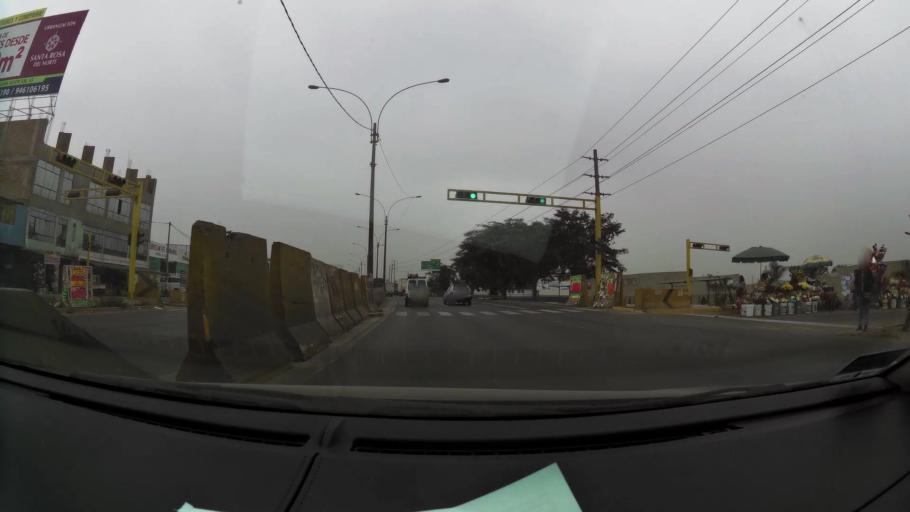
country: PE
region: Lima
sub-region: Lima
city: Urb. Santo Domingo
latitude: -11.8722
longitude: -77.0695
